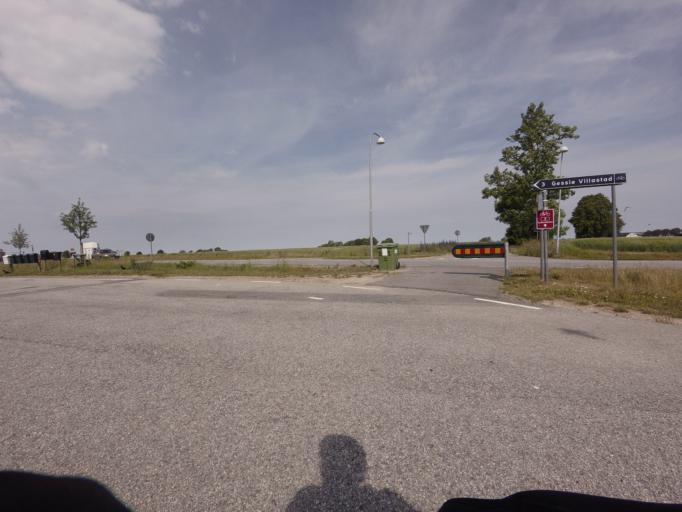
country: SE
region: Skane
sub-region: Malmo
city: Tygelsjo
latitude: 55.5030
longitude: 12.9925
